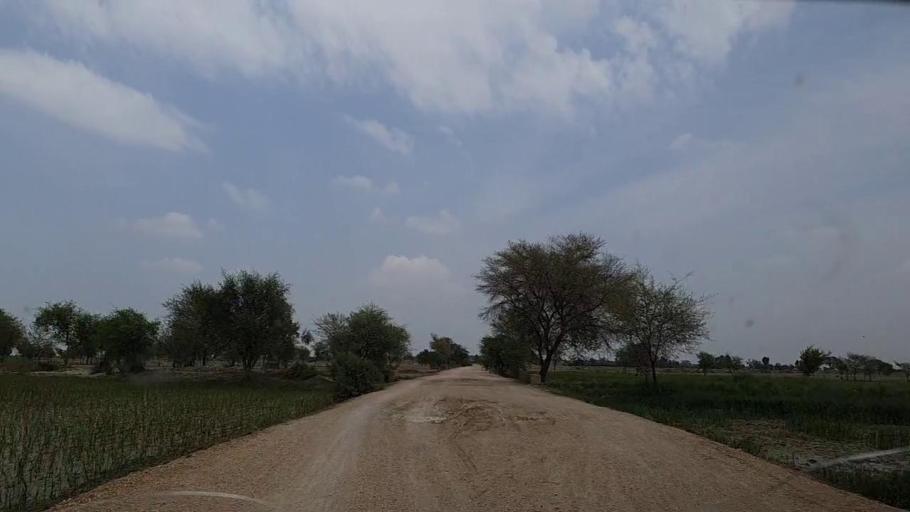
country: PK
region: Sindh
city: Phulji
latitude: 26.8208
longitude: 67.6356
